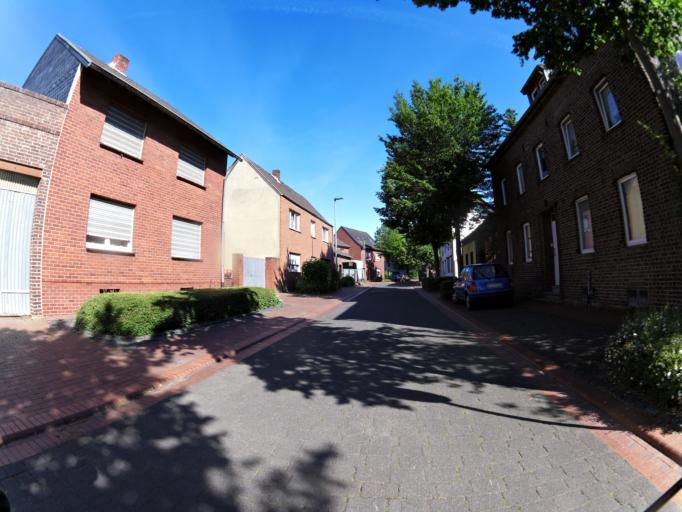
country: DE
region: North Rhine-Westphalia
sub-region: Regierungsbezirk Koln
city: Ubach-Palenberg
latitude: 50.9404
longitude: 6.0558
